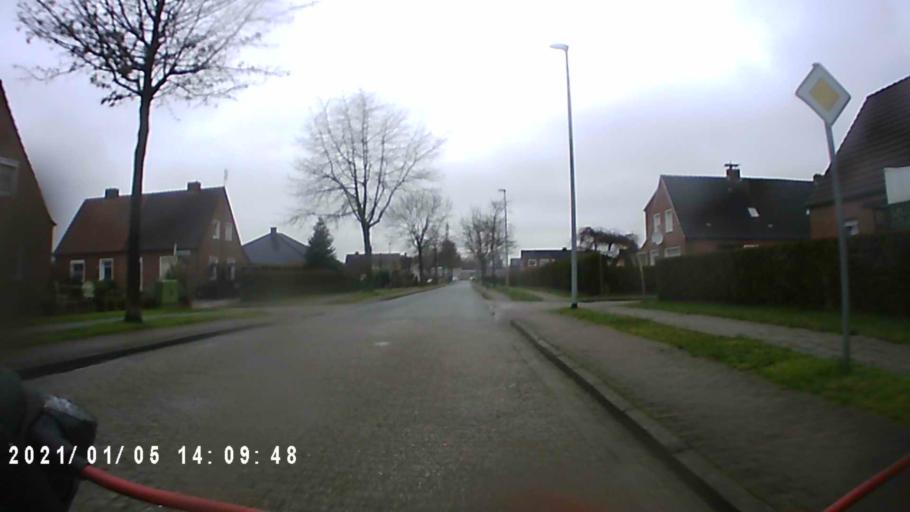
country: DE
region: Lower Saxony
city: Weener
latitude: 53.1664
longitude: 7.3360
